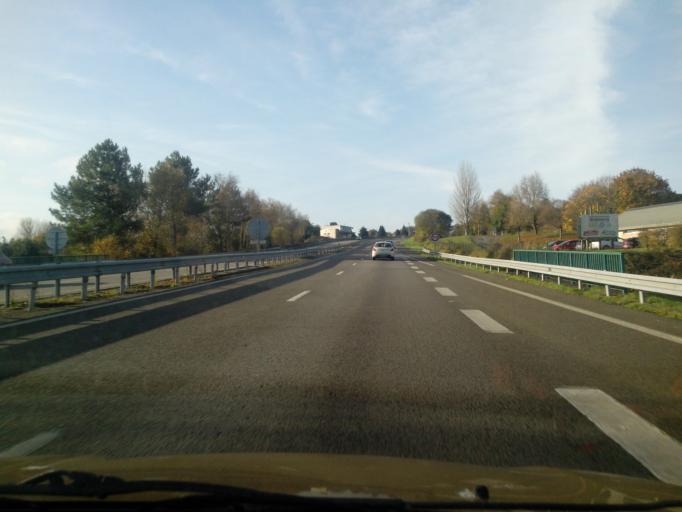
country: FR
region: Brittany
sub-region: Departement du Morbihan
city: Guegon
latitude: 47.9490
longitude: -2.5793
